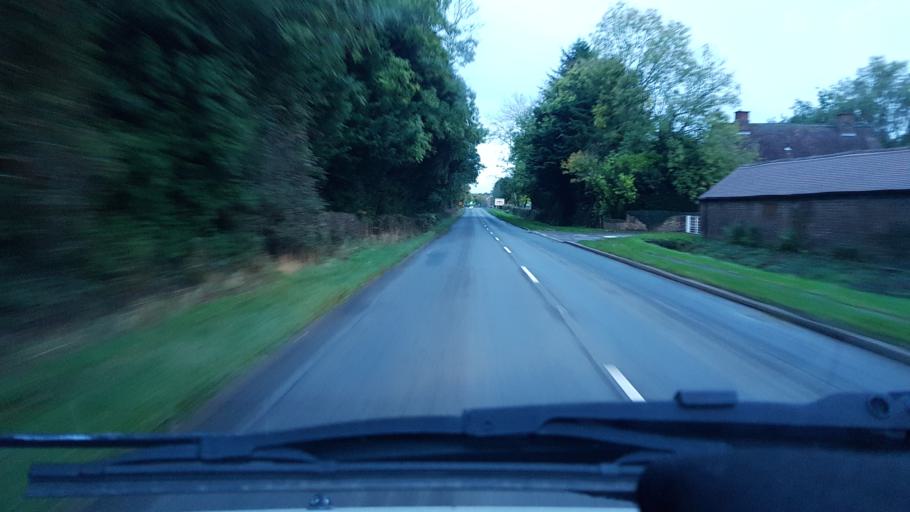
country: GB
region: England
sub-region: Worcestershire
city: Great Malvern
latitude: 52.0836
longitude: -2.3089
